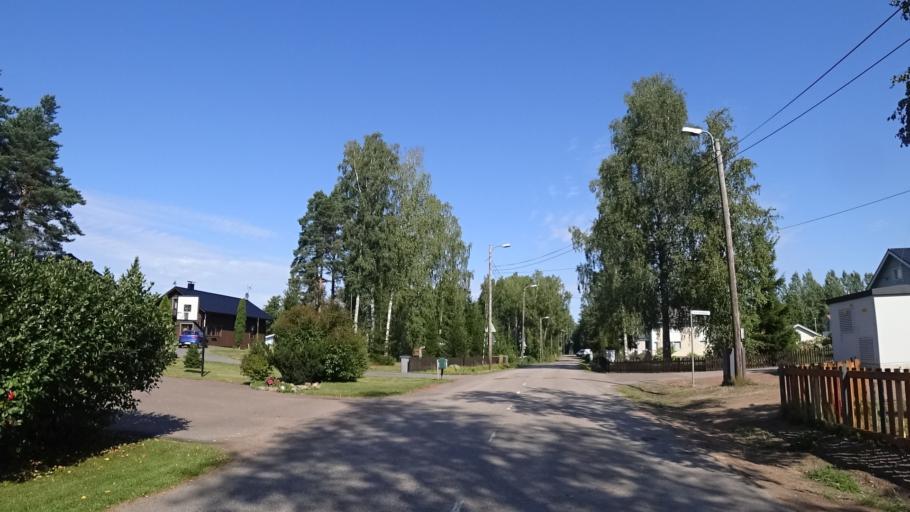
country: FI
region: Kymenlaakso
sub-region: Kotka-Hamina
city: Hamina
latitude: 60.5572
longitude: 27.1996
